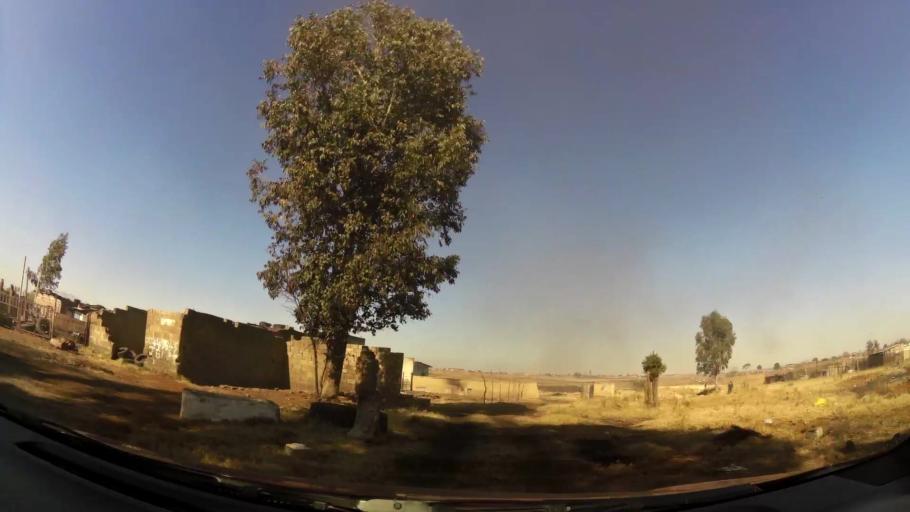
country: ZA
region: Gauteng
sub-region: City of Johannesburg Metropolitan Municipality
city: Soweto
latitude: -26.2171
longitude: 27.8433
